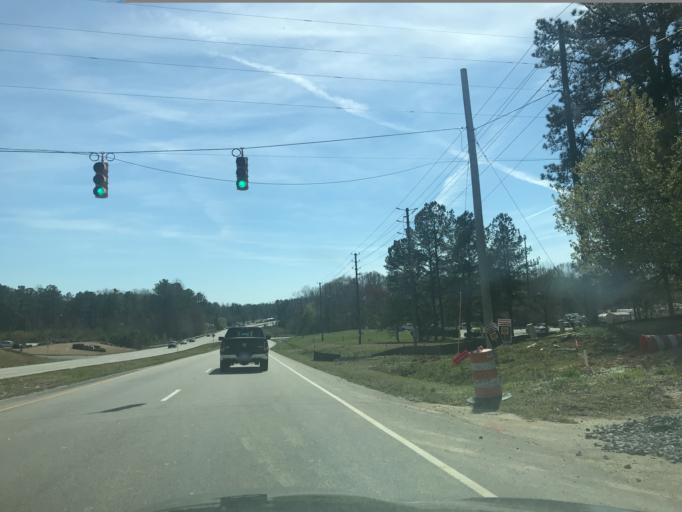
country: US
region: North Carolina
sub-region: Wake County
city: Fuquay-Varina
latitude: 35.6356
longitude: -78.7145
